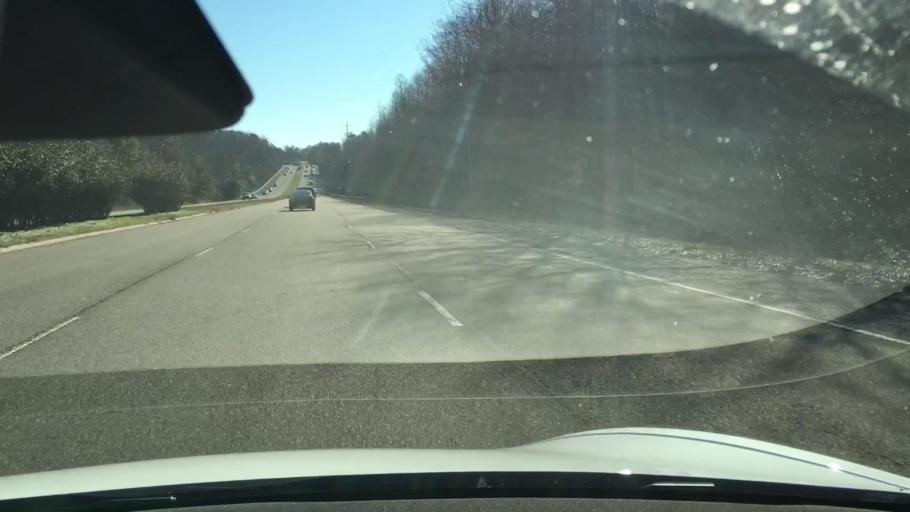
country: US
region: Virginia
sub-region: Chesterfield County
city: Bon Air
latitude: 37.5491
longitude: -77.5650
